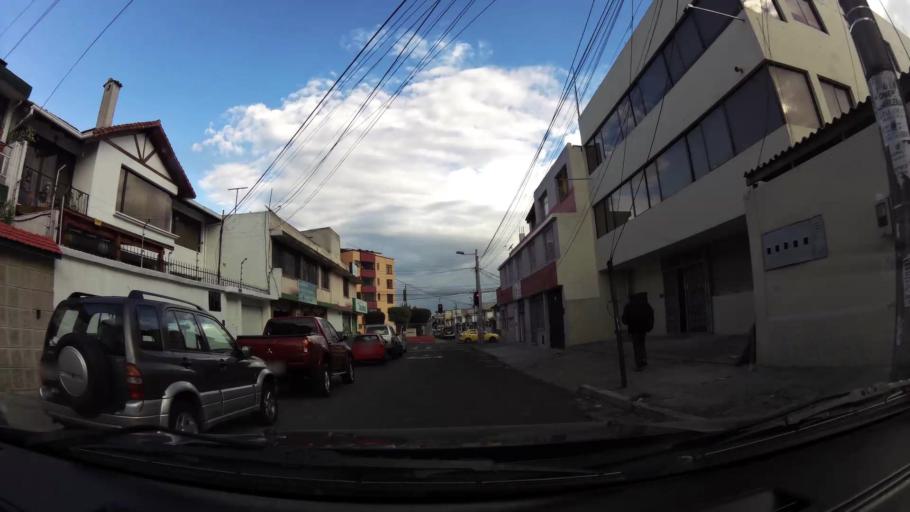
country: EC
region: Pichincha
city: Quito
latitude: -0.1440
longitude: -78.4814
